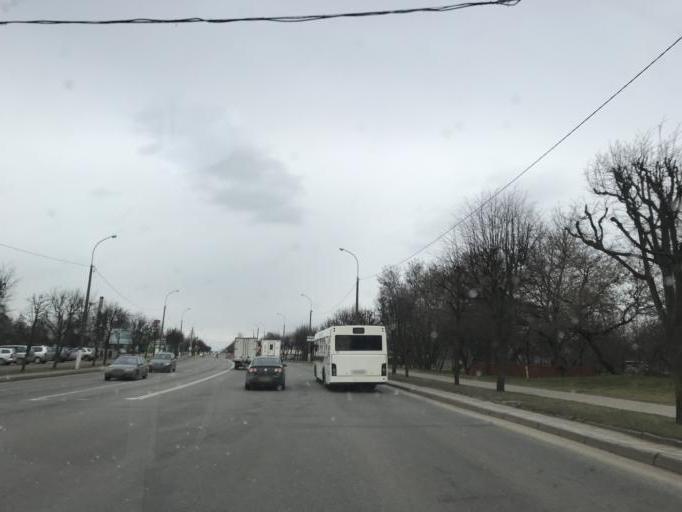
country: BY
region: Mogilev
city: Mahilyow
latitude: 53.9088
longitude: 30.3591
